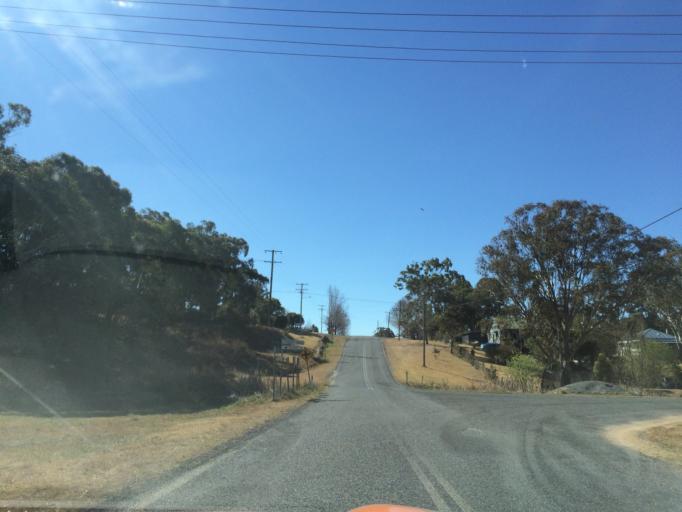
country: AU
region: Queensland
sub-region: Southern Downs
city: Stanthorpe
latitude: -28.6479
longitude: 152.0846
